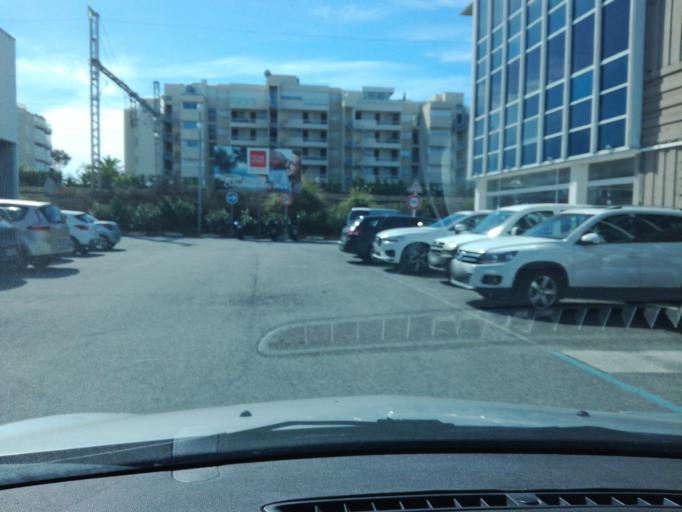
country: FR
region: Provence-Alpes-Cote d'Azur
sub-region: Departement des Alpes-Maritimes
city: Mandelieu-la-Napoule
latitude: 43.5432
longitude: 6.9611
